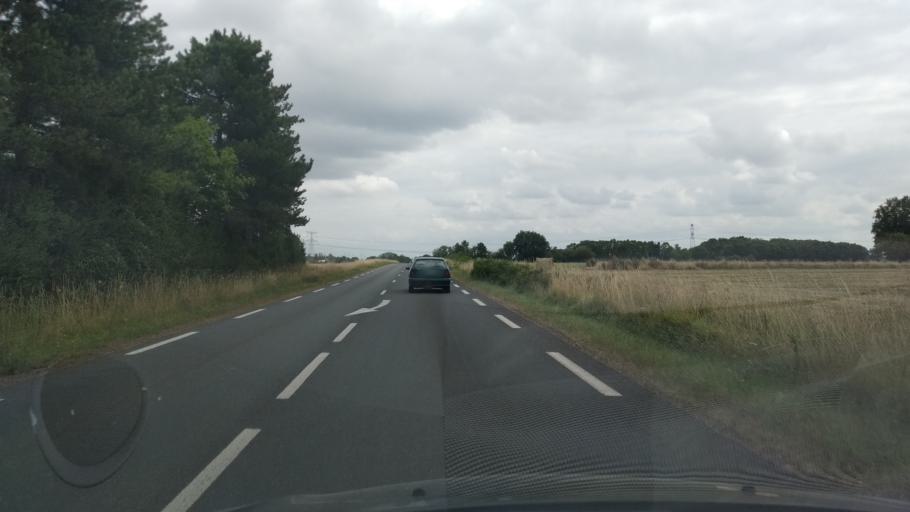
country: FR
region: Poitou-Charentes
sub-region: Departement de la Vienne
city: Saint-Maurice-la-Clouere
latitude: 46.4038
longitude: 0.3926
